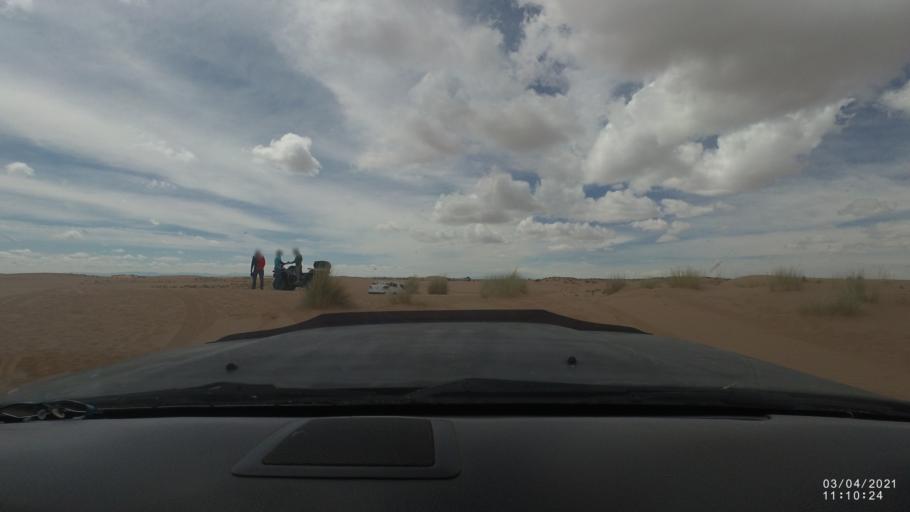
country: BO
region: Oruro
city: Poopo
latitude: -18.7041
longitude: -67.5189
